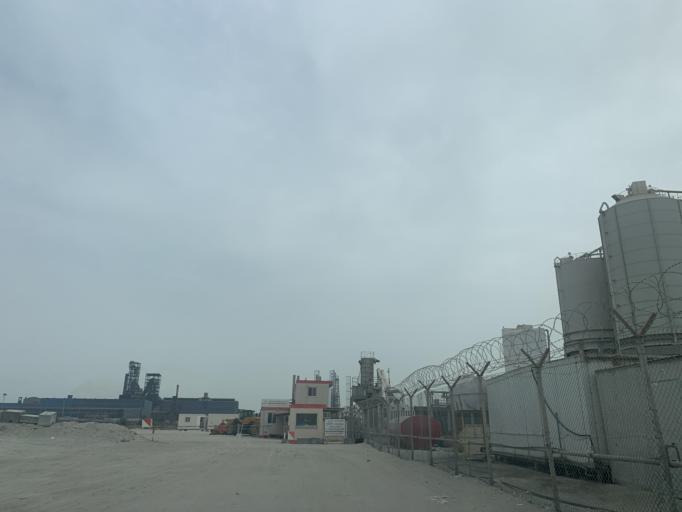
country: BH
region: Muharraq
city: Al Hadd
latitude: 26.2042
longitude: 50.6710
